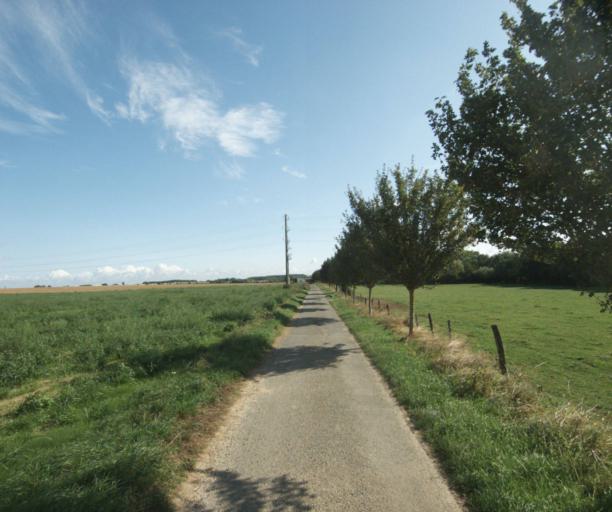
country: FR
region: Nord-Pas-de-Calais
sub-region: Departement du Nord
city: Anstaing
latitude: 50.5924
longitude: 3.1882
